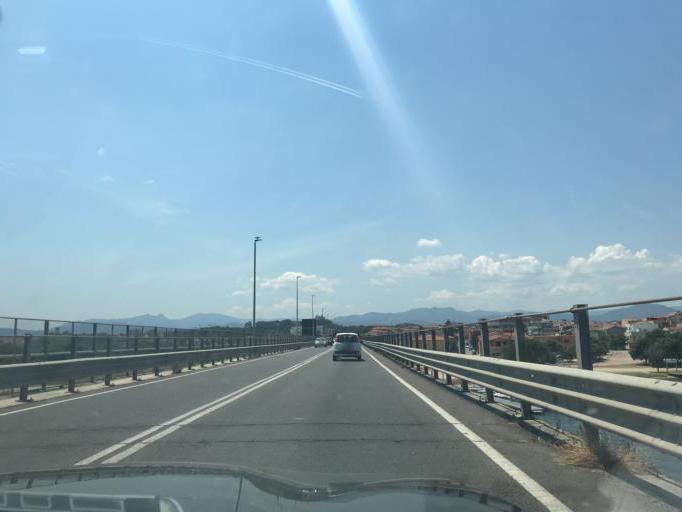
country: IT
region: Sardinia
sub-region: Provincia di Olbia-Tempio
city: Olbia
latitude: 40.9189
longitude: 9.5014
